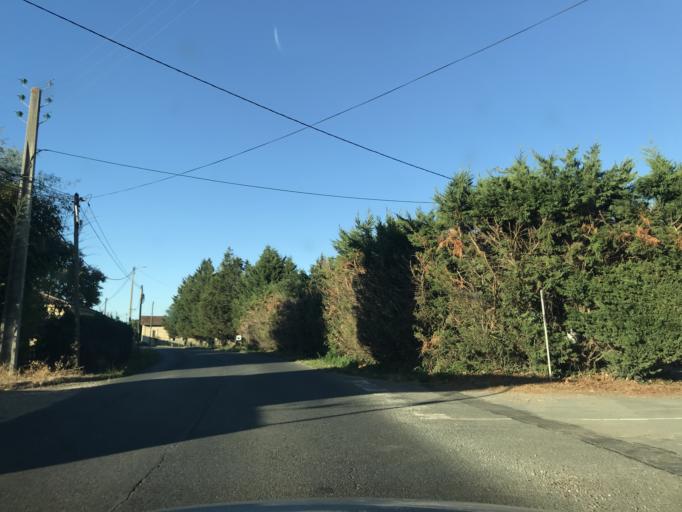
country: FR
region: Aquitaine
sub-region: Departement de la Gironde
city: Mouliets-et-Villemartin
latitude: 44.8293
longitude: -0.0407
